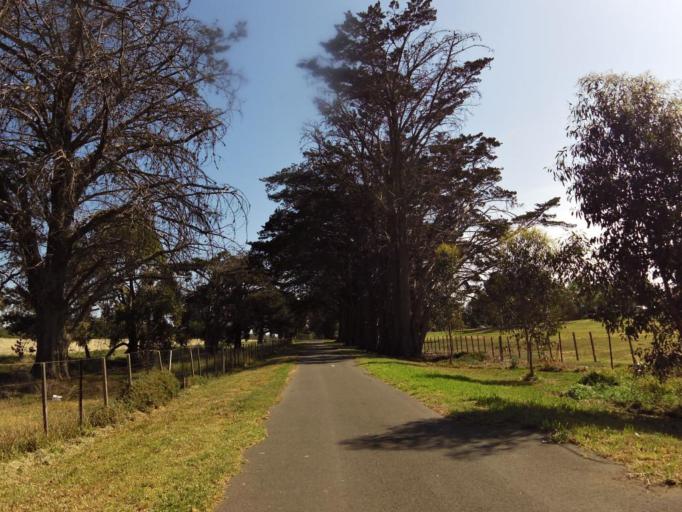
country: AU
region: Victoria
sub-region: Wyndham
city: Werribee
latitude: -37.9139
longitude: 144.6735
